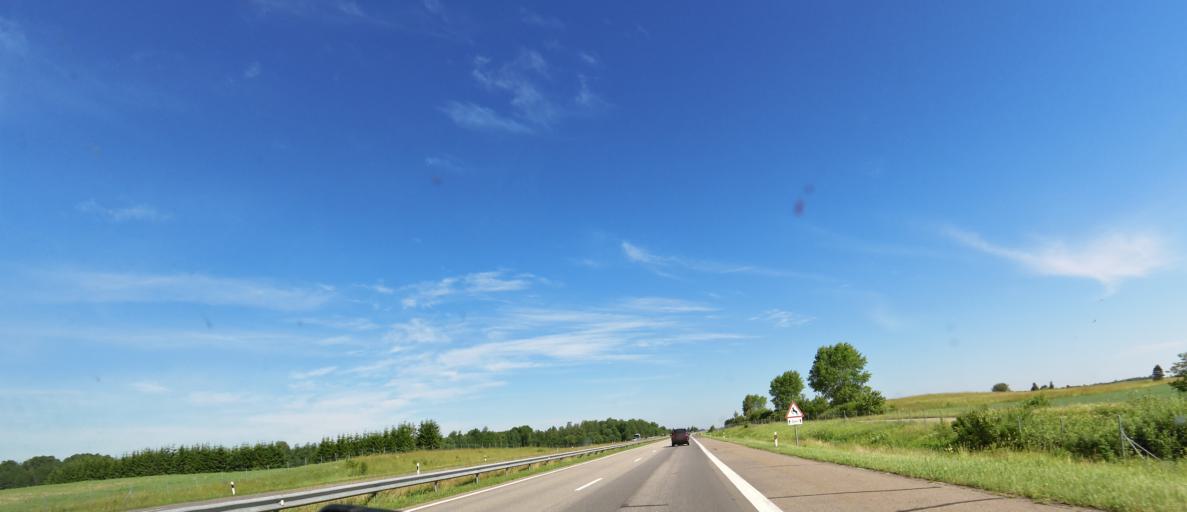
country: LT
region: Vilnius County
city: Ukmerge
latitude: 55.1710
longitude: 24.8147
